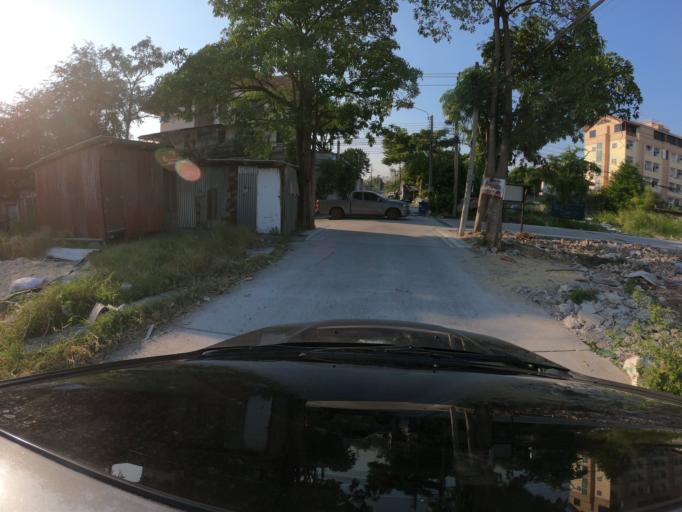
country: TH
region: Bangkok
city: Bang Na
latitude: 13.6449
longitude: 100.6348
